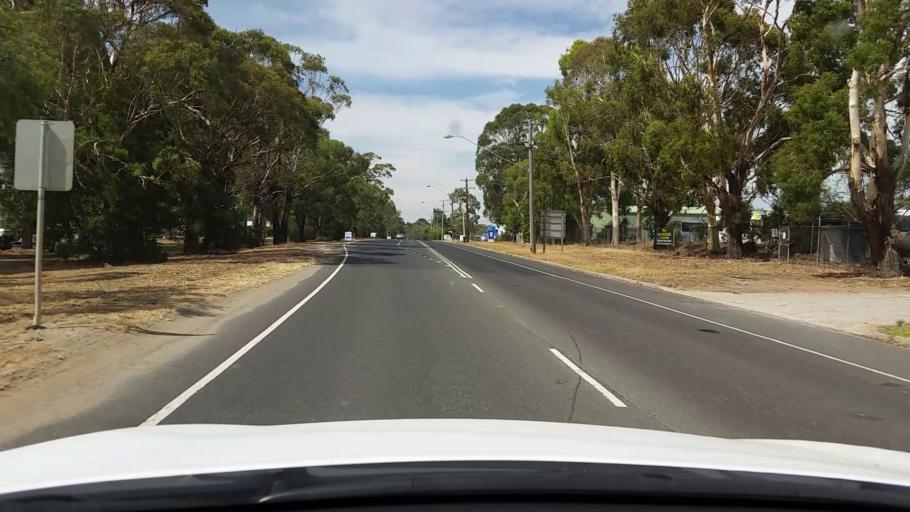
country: AU
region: Victoria
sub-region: Mornington Peninsula
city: Hastings
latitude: -38.3113
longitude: 145.1836
